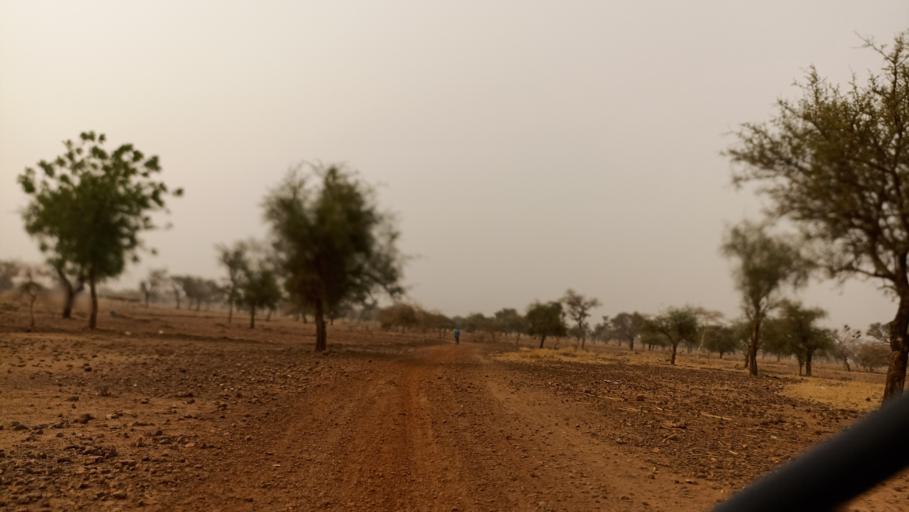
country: BF
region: Nord
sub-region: Province du Zondoma
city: Gourcy
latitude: 13.2388
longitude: -2.5850
